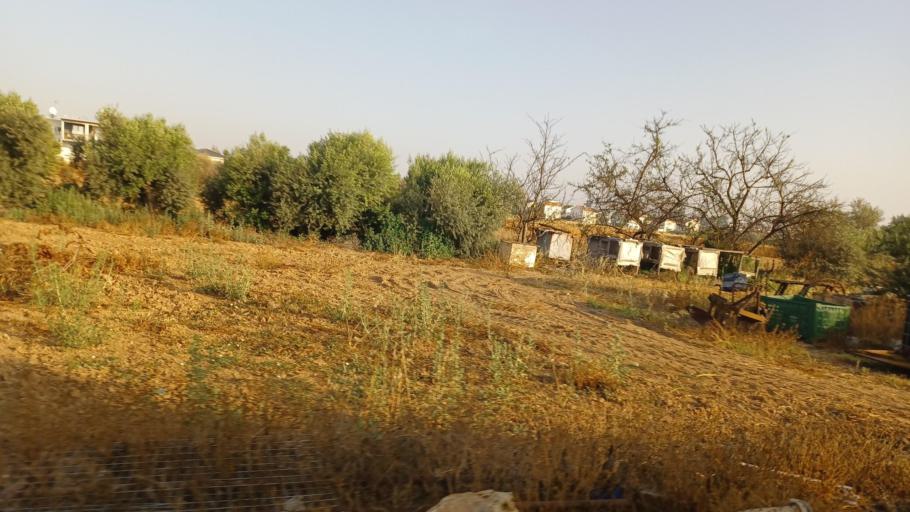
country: CY
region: Ammochostos
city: Paralimni
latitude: 35.0290
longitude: 33.9570
